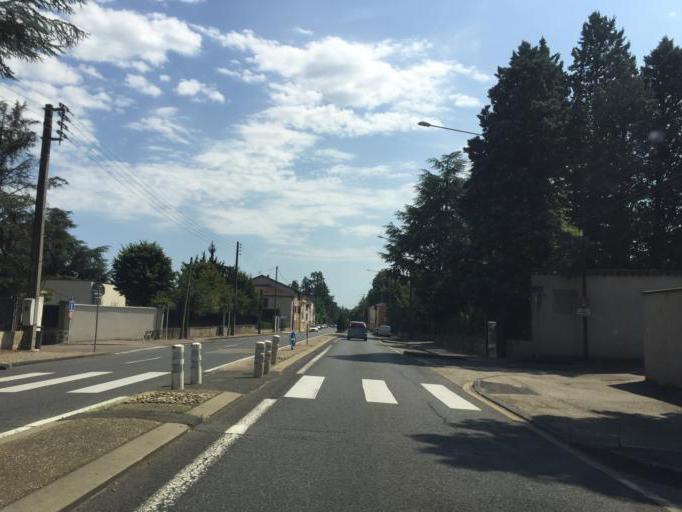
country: FR
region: Rhone-Alpes
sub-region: Departement du Rhone
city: Charbonnieres-les-Bains
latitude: 45.7760
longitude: 4.7520
